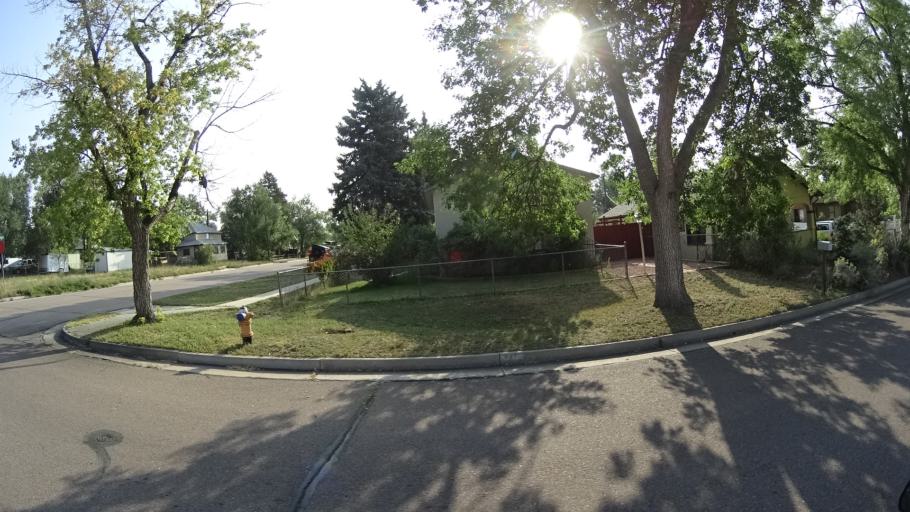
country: US
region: Colorado
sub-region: El Paso County
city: Colorado Springs
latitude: 38.8436
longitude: -104.7915
